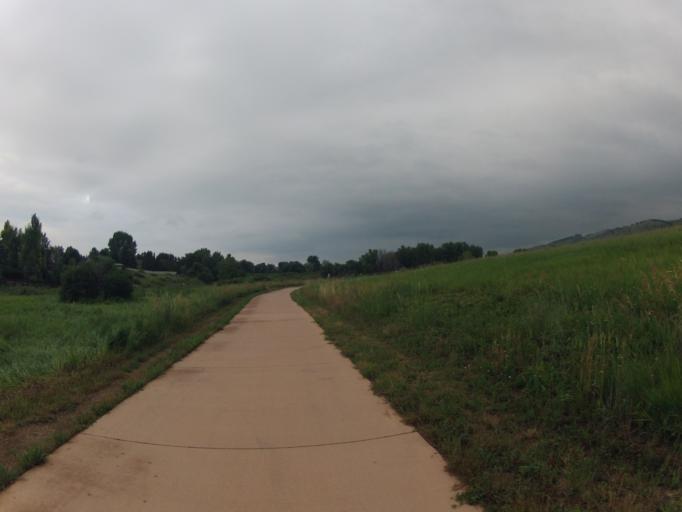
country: US
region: Colorado
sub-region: Larimer County
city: Fort Collins
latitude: 40.5350
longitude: -105.1272
